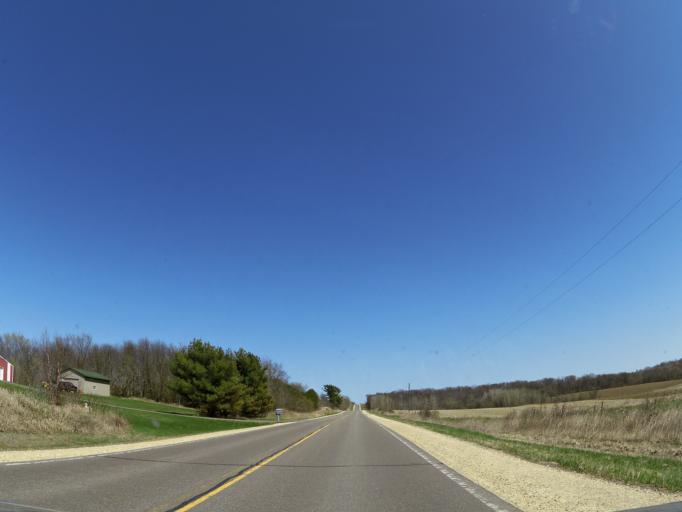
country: US
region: Wisconsin
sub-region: Saint Croix County
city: Hammond
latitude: 44.9344
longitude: -92.4522
